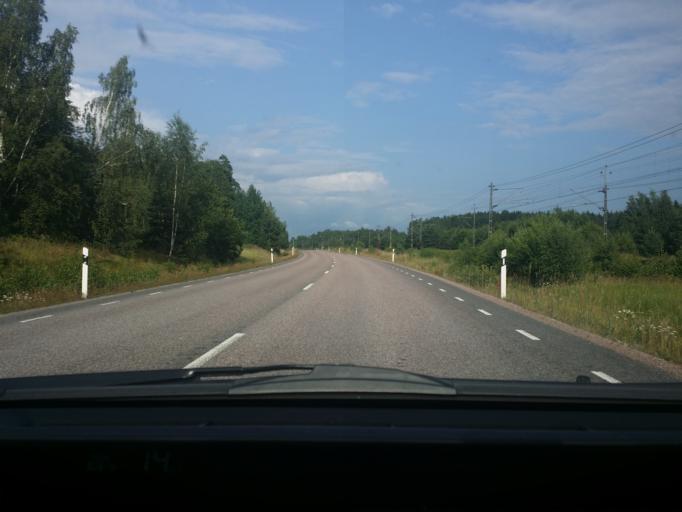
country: SE
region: Vaestmanland
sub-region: Hallstahammars Kommun
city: Kolback
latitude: 59.5662
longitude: 16.3653
